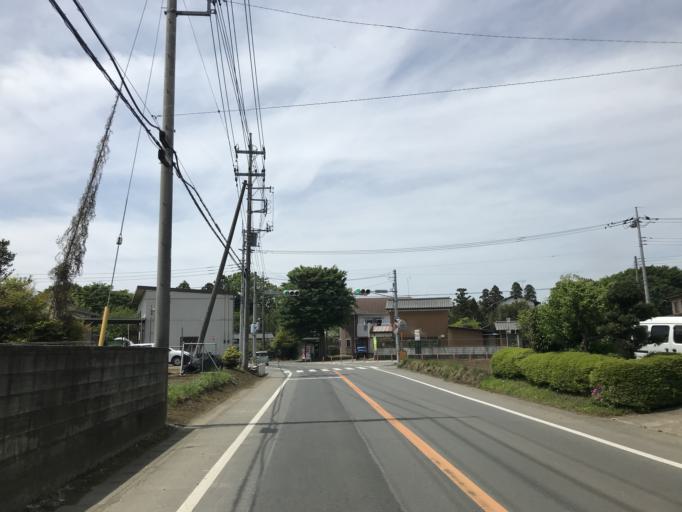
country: JP
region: Ibaraki
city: Mitsukaido
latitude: 35.9930
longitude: 139.9586
